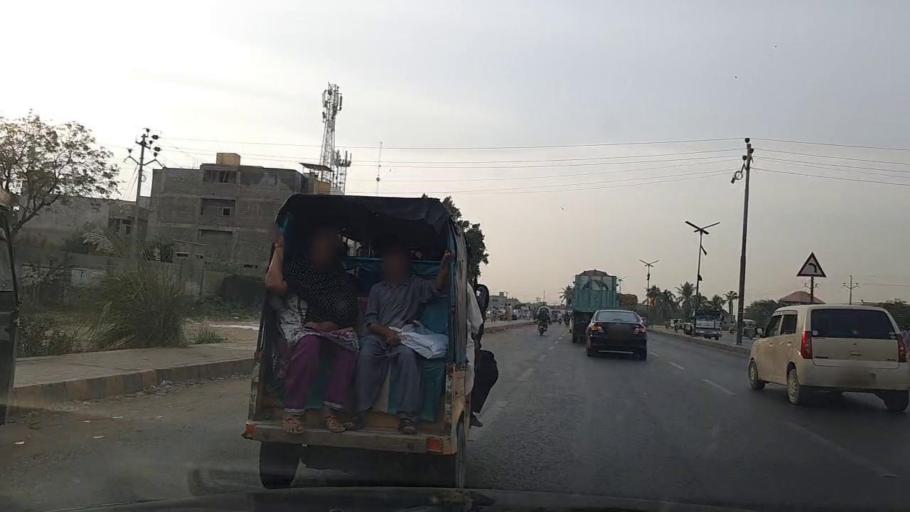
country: PK
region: Sindh
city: Malir Cantonment
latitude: 24.8539
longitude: 67.2449
